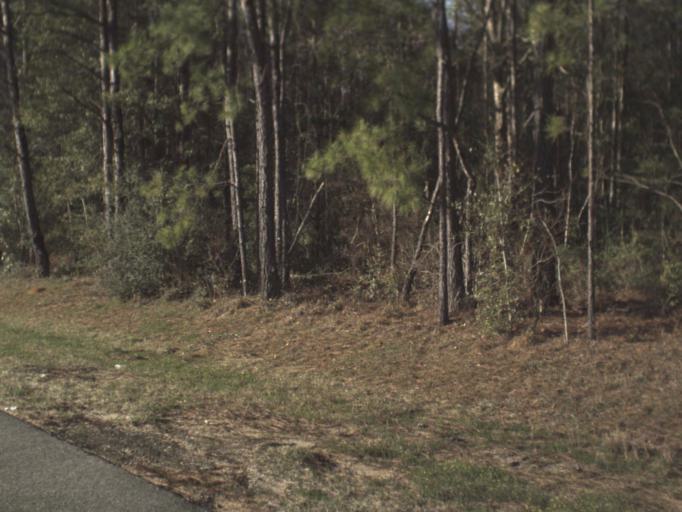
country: US
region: Florida
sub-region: Jackson County
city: Marianna
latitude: 30.6643
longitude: -85.2268
